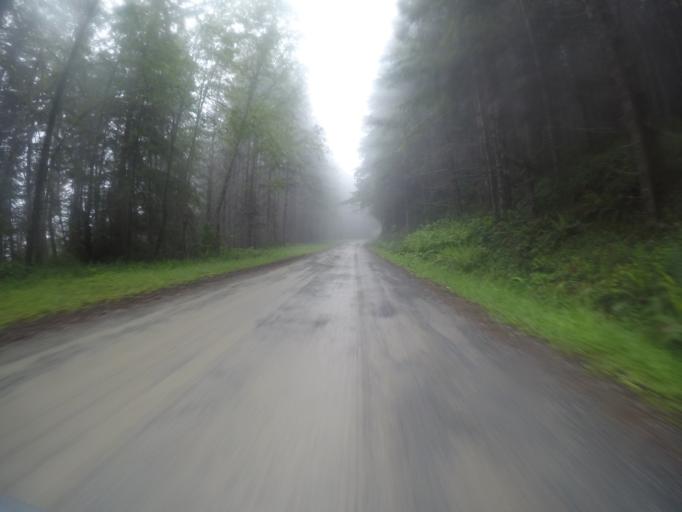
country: US
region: California
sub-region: Humboldt County
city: Westhaven-Moonstone
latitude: 41.2387
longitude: -123.9941
